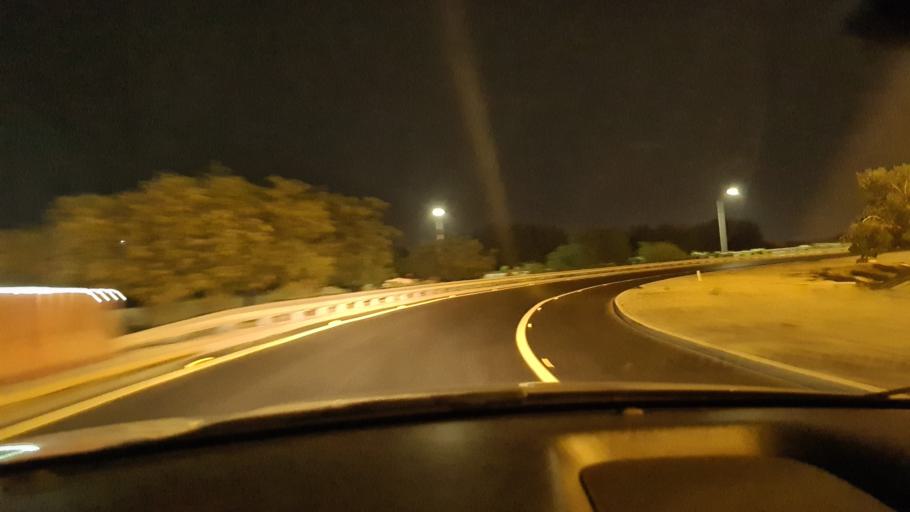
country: SA
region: Eastern Province
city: Al Jubayl
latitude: 27.1378
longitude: 49.5585
